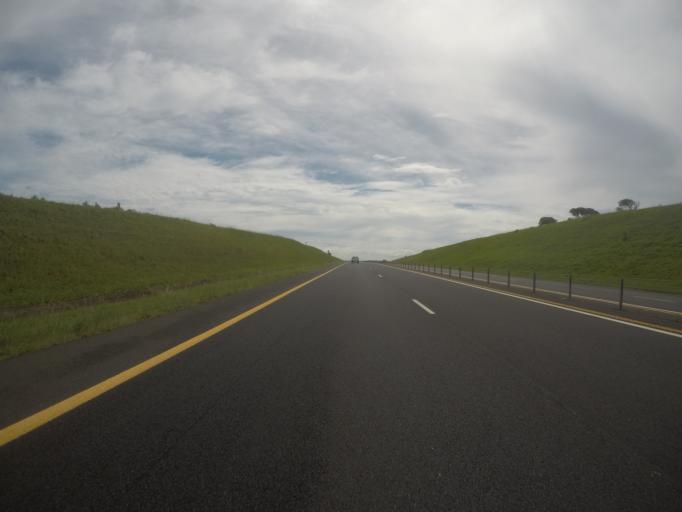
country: ZA
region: KwaZulu-Natal
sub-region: iLembe District Municipality
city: Mandeni
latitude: -29.0634
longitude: 31.6249
